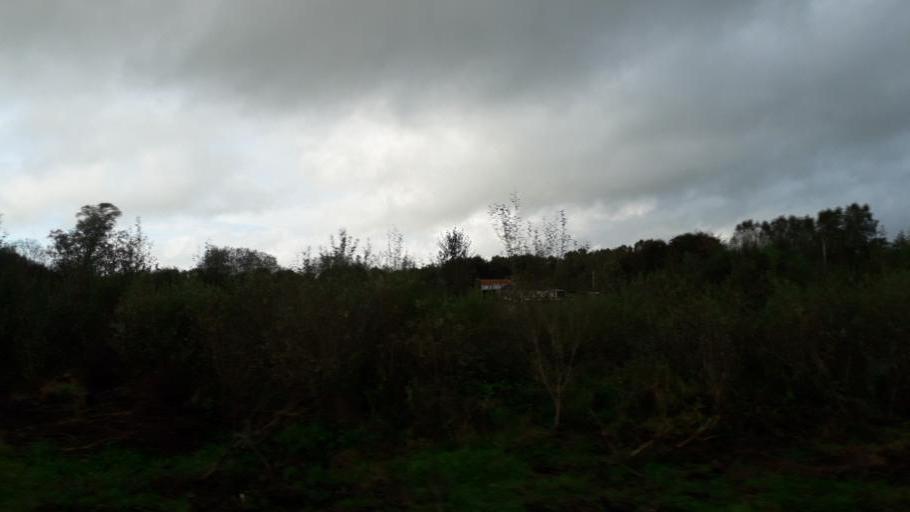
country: IE
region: Leinster
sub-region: An Longfort
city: Lanesborough
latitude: 53.7658
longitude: -8.0806
